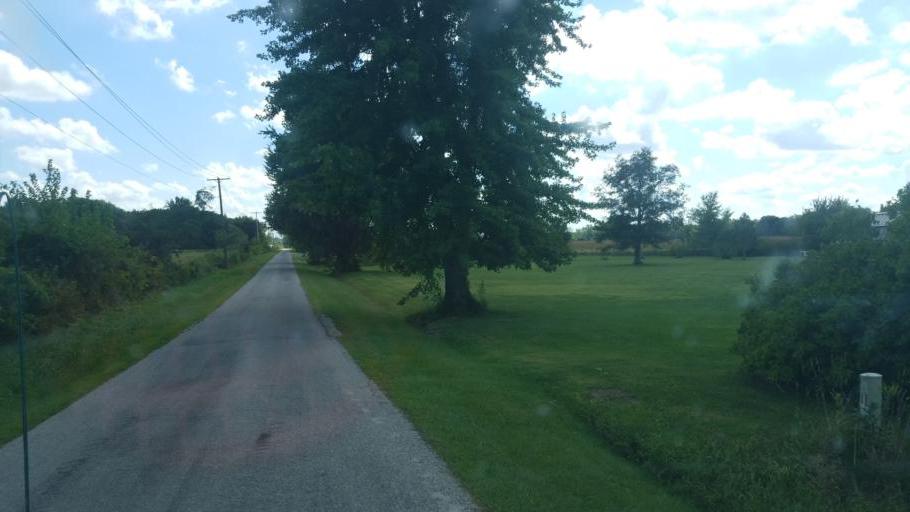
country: US
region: Ohio
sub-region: Union County
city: Richwood
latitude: 40.3515
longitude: -83.2433
